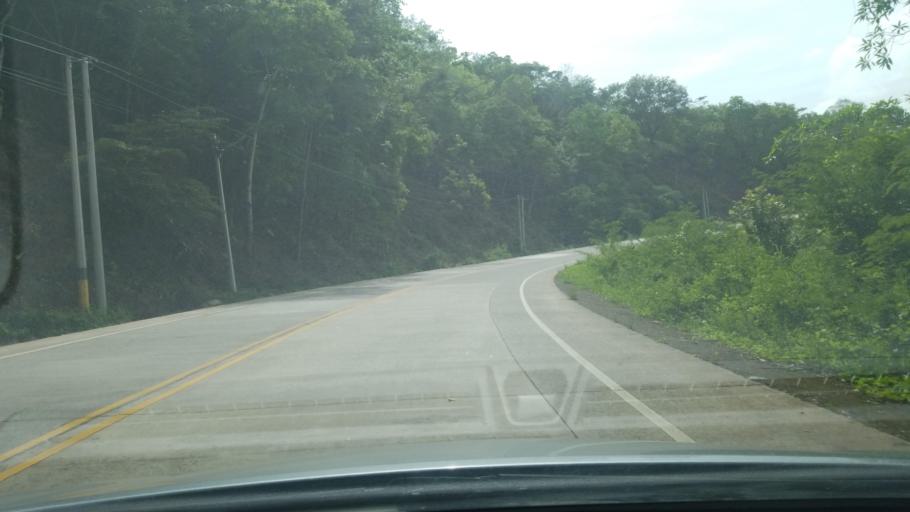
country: HN
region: Copan
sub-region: Santa Rita
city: Santa Rita, Copan
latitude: 14.8708
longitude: -89.0649
